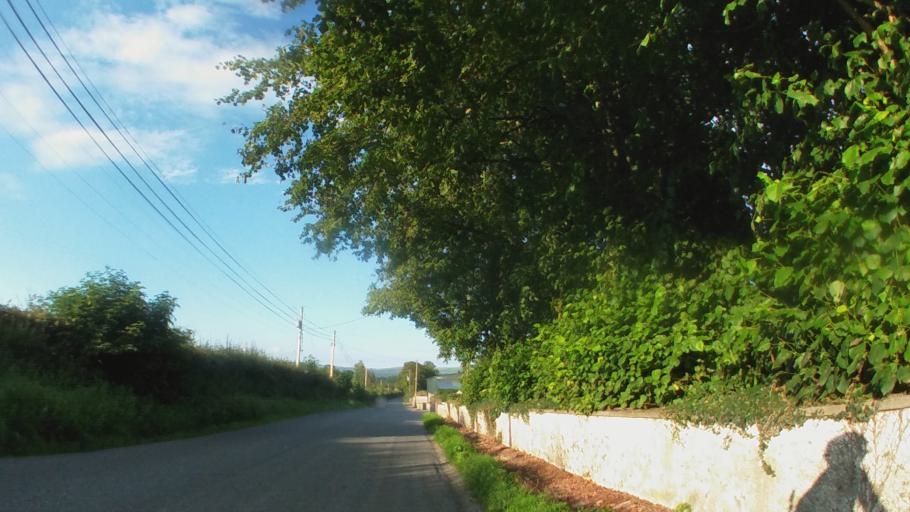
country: IE
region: Leinster
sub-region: Kilkenny
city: Kilkenny
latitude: 52.6704
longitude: -7.2114
